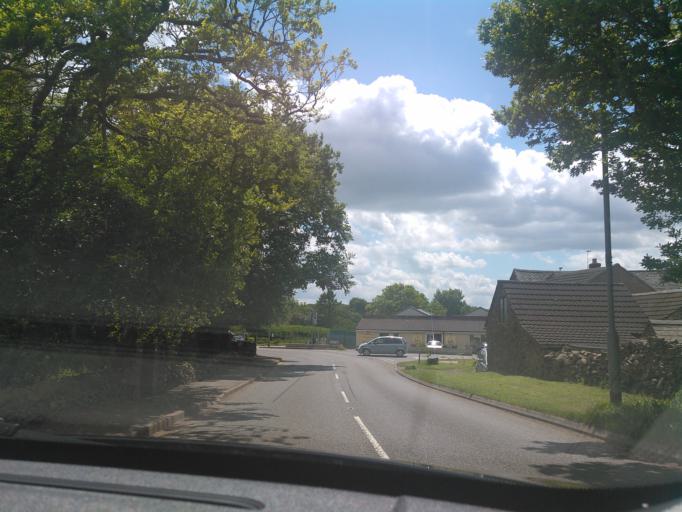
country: GB
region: England
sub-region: Leicestershire
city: Markfield
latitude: 52.6923
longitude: -1.2818
